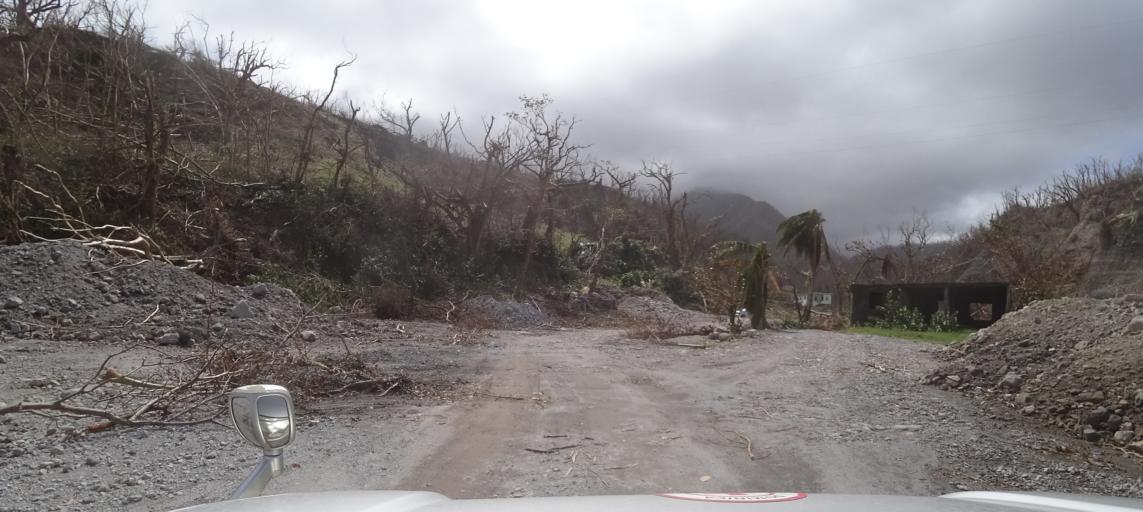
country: DM
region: Saint Patrick
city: La Plaine
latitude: 15.3205
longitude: -61.2446
